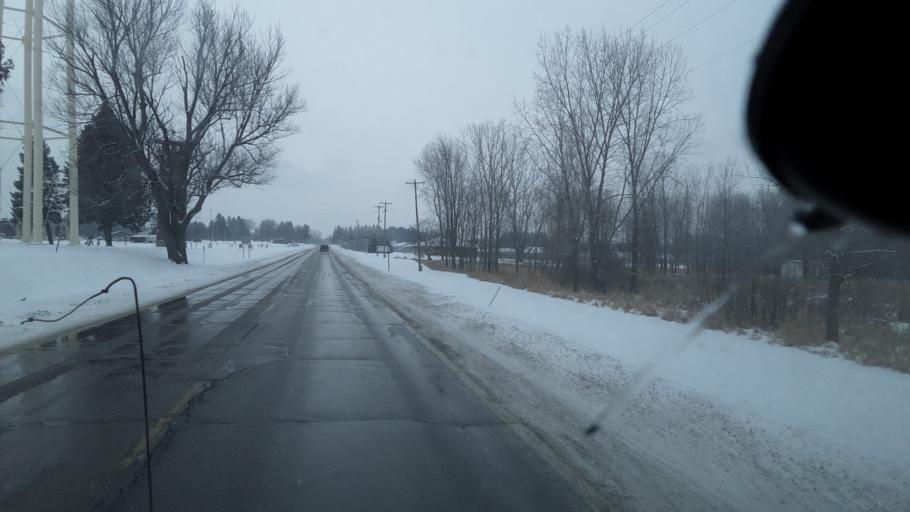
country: US
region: Michigan
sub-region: Jackson County
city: Jackson
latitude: 42.2997
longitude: -84.3923
